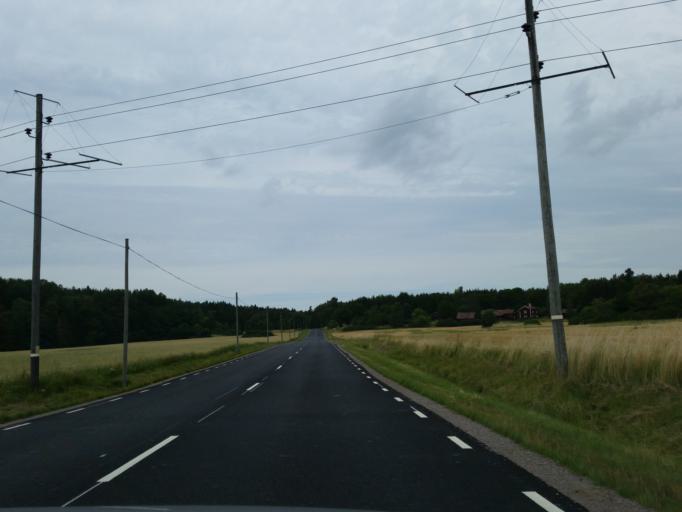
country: SE
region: Soedermanland
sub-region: Strangnas Kommun
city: Mariefred
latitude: 59.2584
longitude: 17.1725
